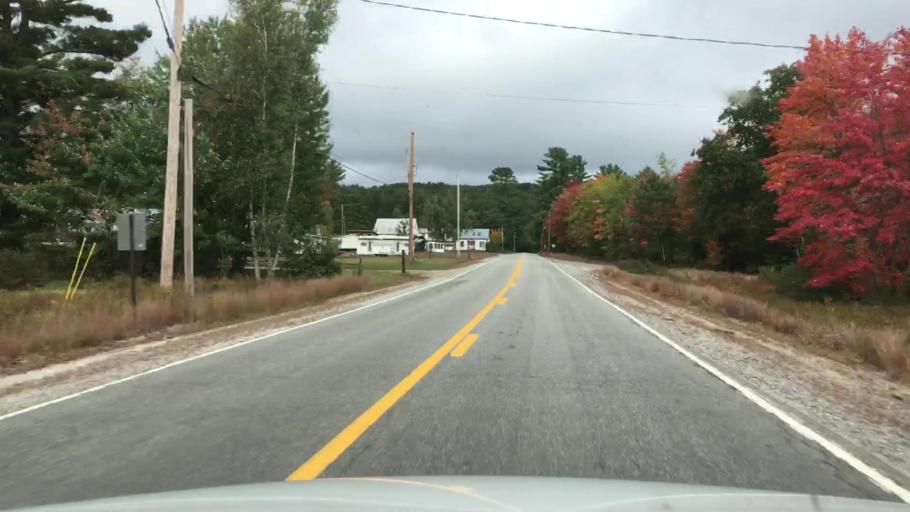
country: US
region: Maine
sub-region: Oxford County
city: Bethel
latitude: 44.3463
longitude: -70.7865
